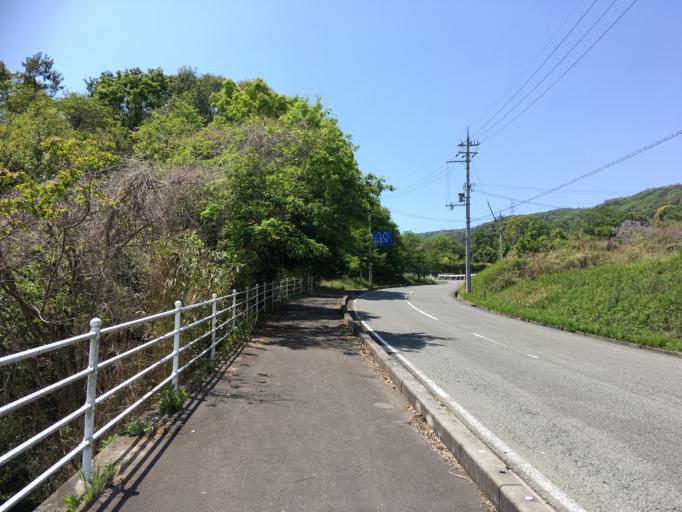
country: JP
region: Nara
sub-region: Ikoma-shi
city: Ikoma
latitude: 34.6536
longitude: 135.6936
